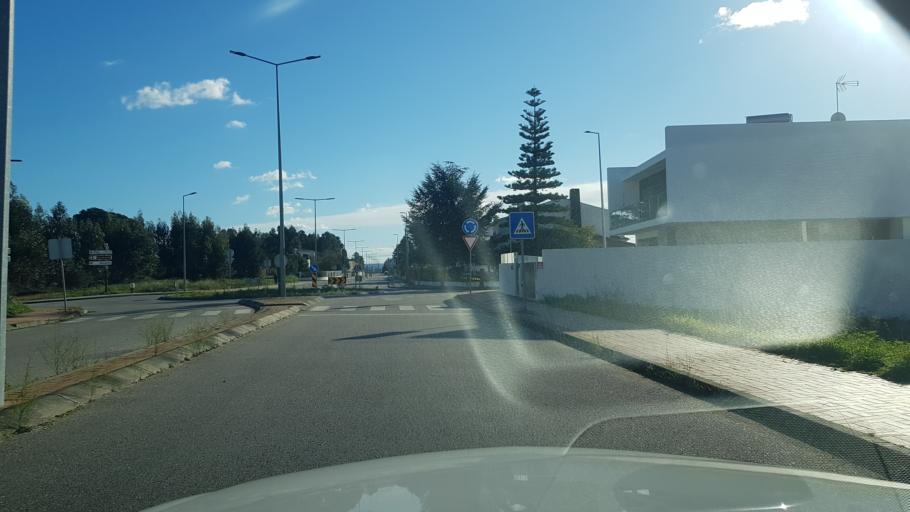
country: PT
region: Santarem
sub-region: Entroncamento
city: Entroncamento
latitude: 39.4821
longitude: -8.4689
